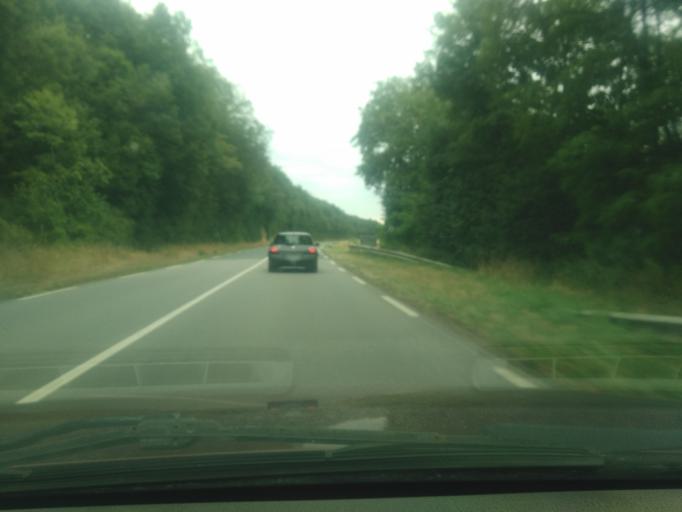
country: FR
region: Centre
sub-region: Departement de l'Indre
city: Le Blanc
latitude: 46.6337
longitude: 1.1098
